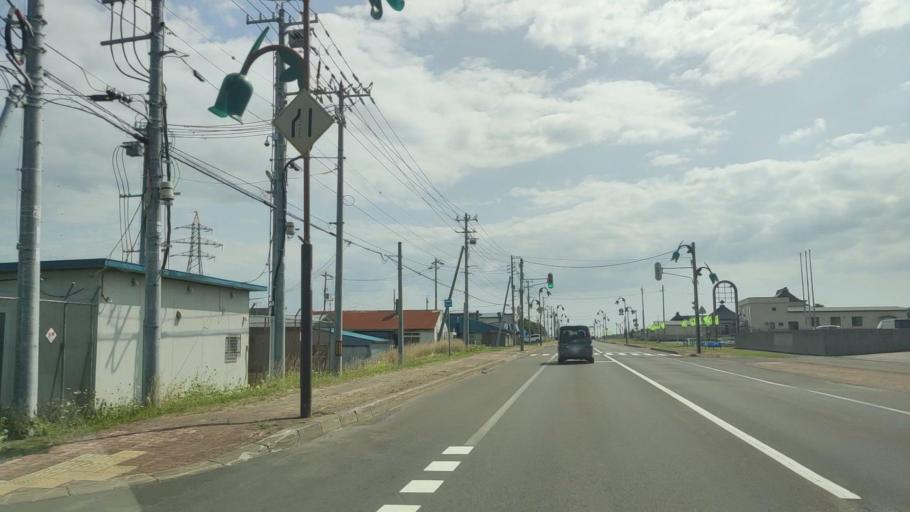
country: JP
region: Hokkaido
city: Rumoi
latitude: 44.3063
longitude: 141.6538
